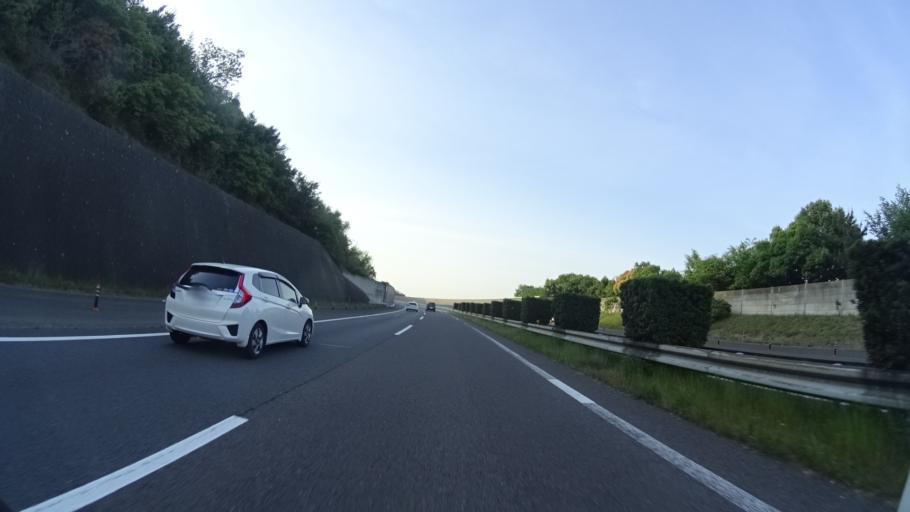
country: JP
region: Kagawa
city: Sakaidecho
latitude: 34.3121
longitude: 133.8394
